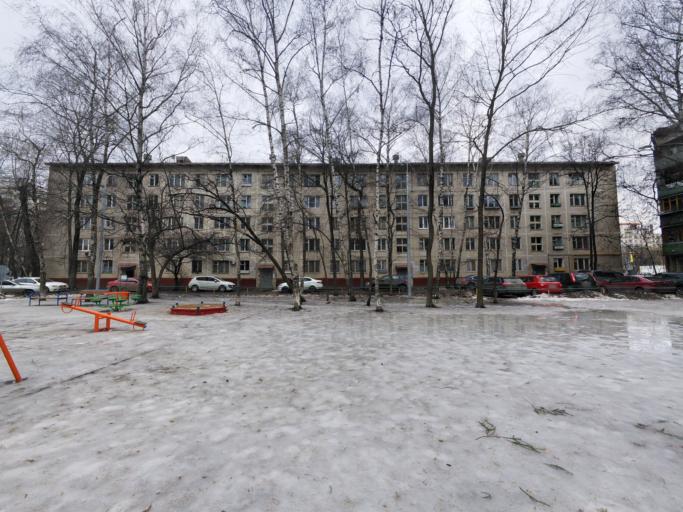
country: RU
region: Moscow
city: Likhobory
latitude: 55.8110
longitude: 37.5698
